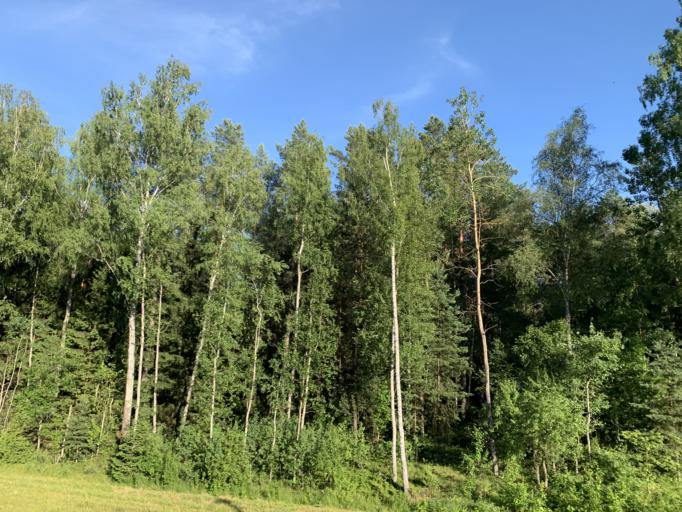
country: BY
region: Minsk
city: Enyerhyetykaw
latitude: 53.5313
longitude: 26.9367
